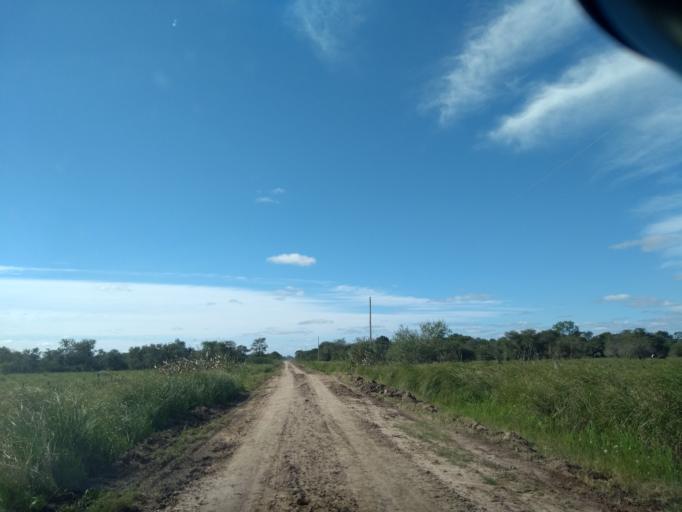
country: AR
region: Chaco
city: Colonia Benitez
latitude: -27.2882
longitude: -58.9326
